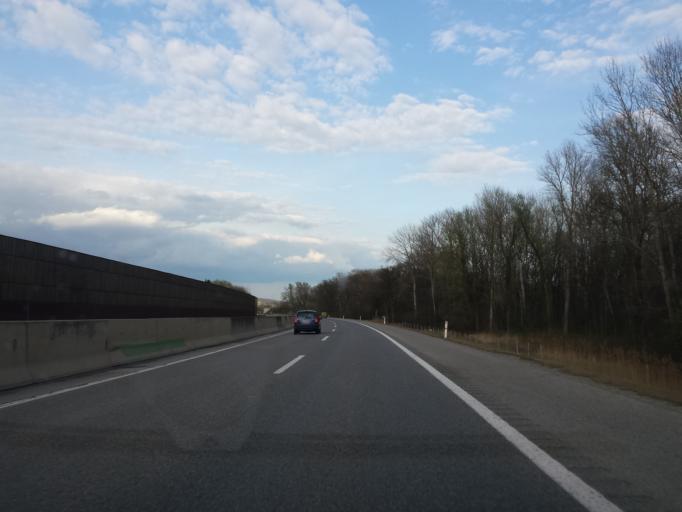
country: AT
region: Lower Austria
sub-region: Politischer Bezirk Korneuburg
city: Stockerau
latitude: 48.3788
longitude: 16.1735
